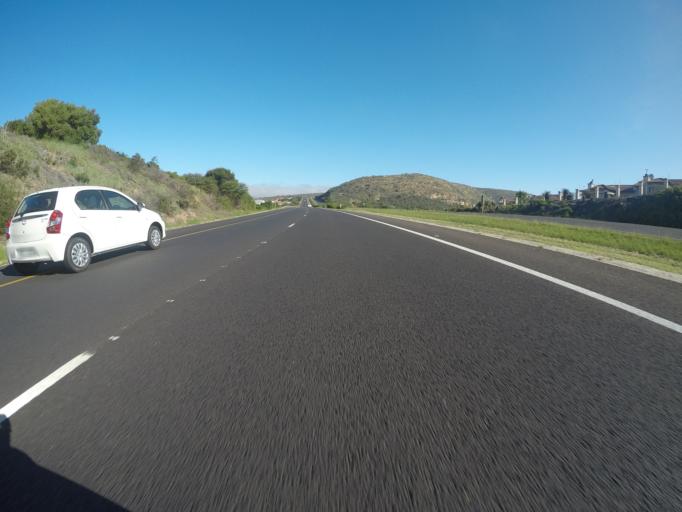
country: ZA
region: Western Cape
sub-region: Eden District Municipality
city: Mossel Bay
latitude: -34.1489
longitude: 22.0987
